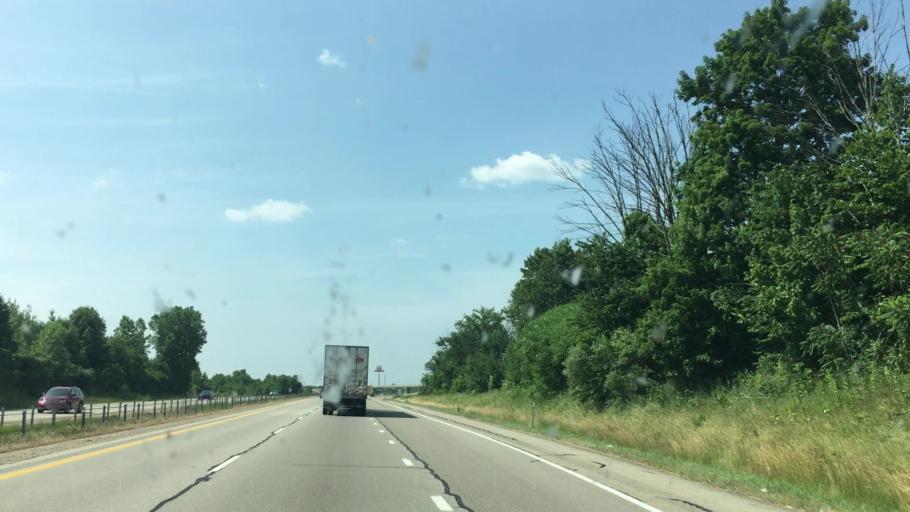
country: US
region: Michigan
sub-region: Allegan County
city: Wayland
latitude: 42.7196
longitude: -85.6687
